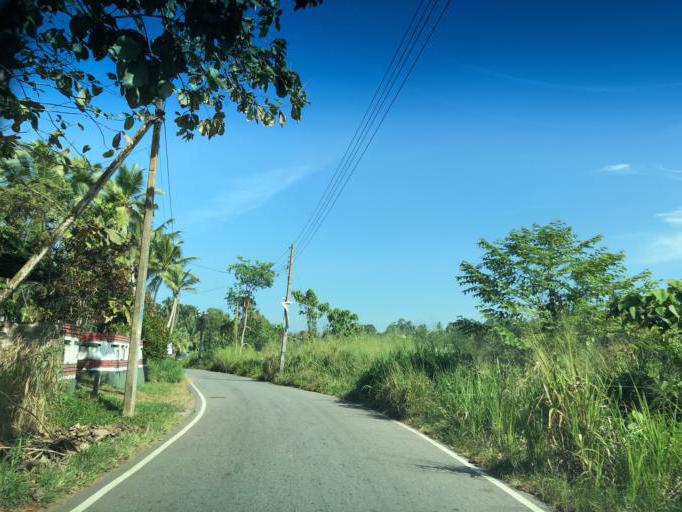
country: LK
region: Western
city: Homagama
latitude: 6.7995
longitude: 79.9818
